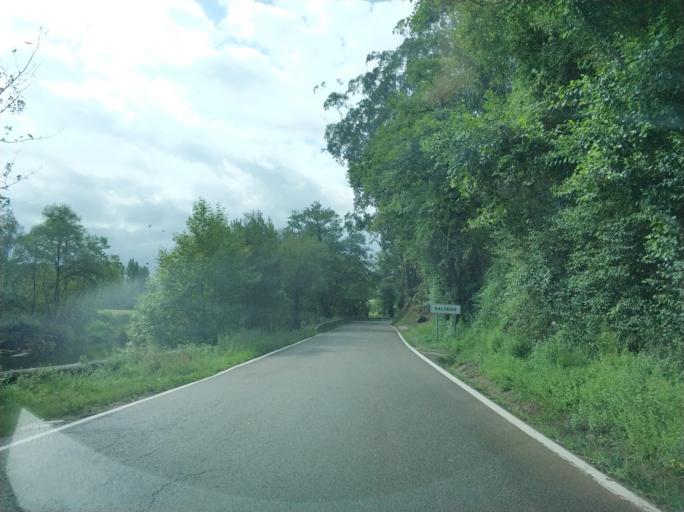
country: ES
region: Cantabria
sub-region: Provincia de Cantabria
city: Polanco
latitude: 43.3745
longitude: -3.9711
